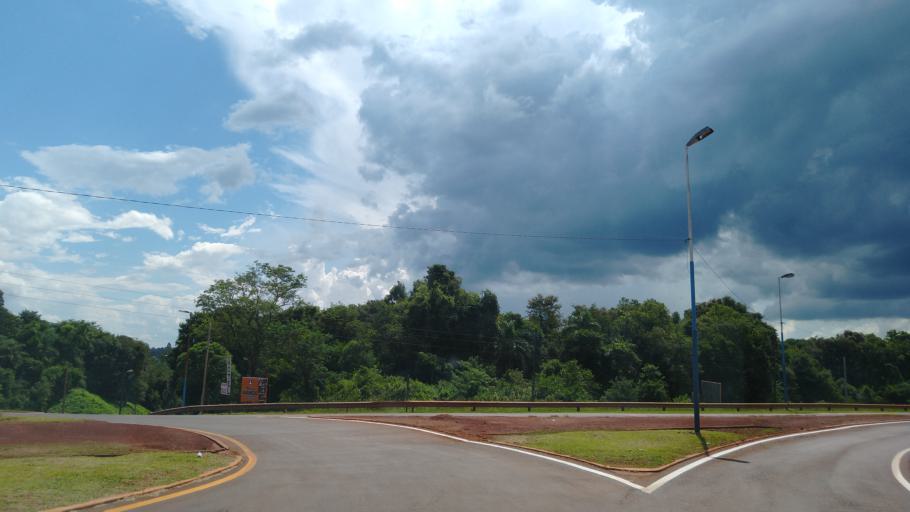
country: AR
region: Misiones
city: Puerto Libertad
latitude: -25.9697
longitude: -54.5791
